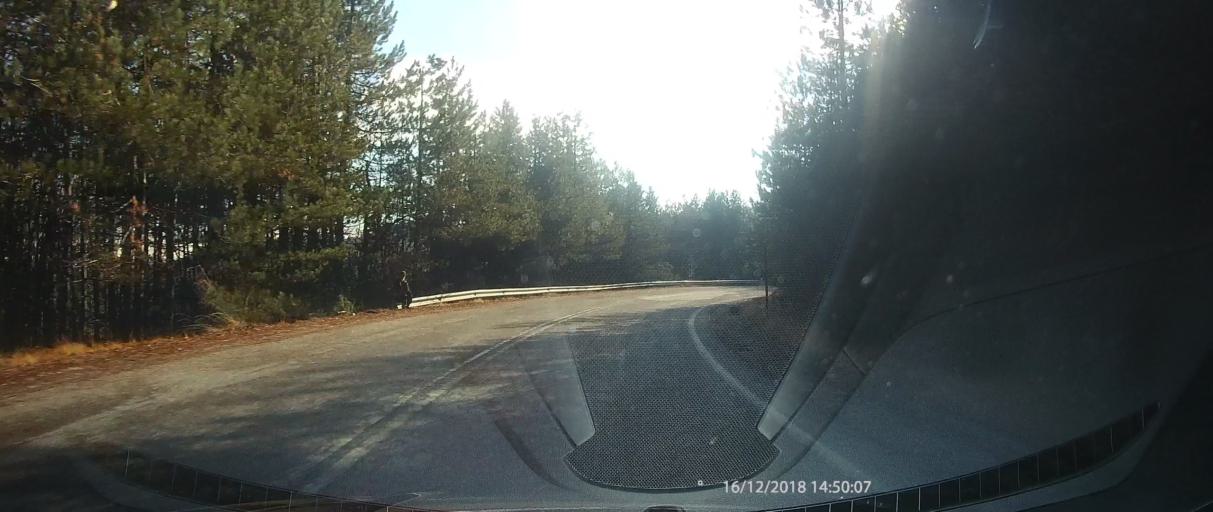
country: GR
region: West Macedonia
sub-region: Nomos Kastorias
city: Nestorio
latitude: 40.2079
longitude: 21.0829
